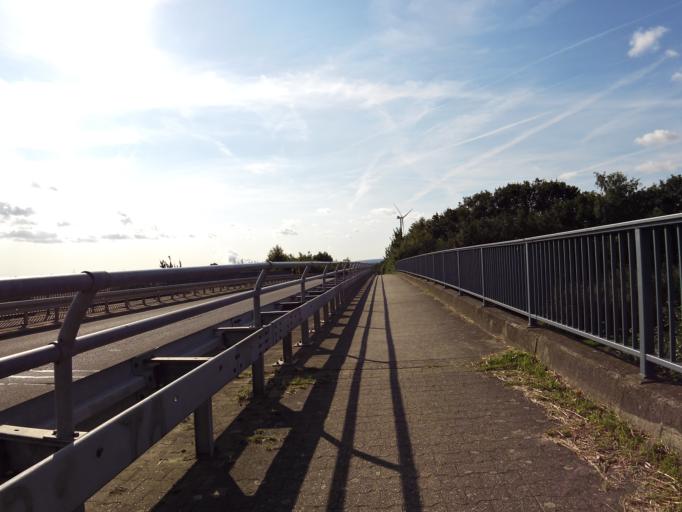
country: DE
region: North Rhine-Westphalia
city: Niedermerz
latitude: 50.8805
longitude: 6.2448
